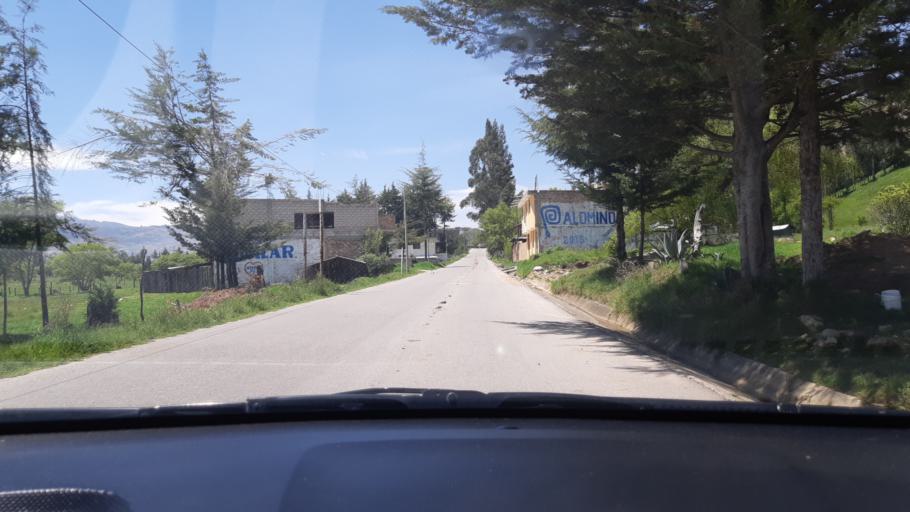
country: PE
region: Cajamarca
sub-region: Provincia de Cajamarca
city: Llacanora
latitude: -7.1813
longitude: -78.4539
